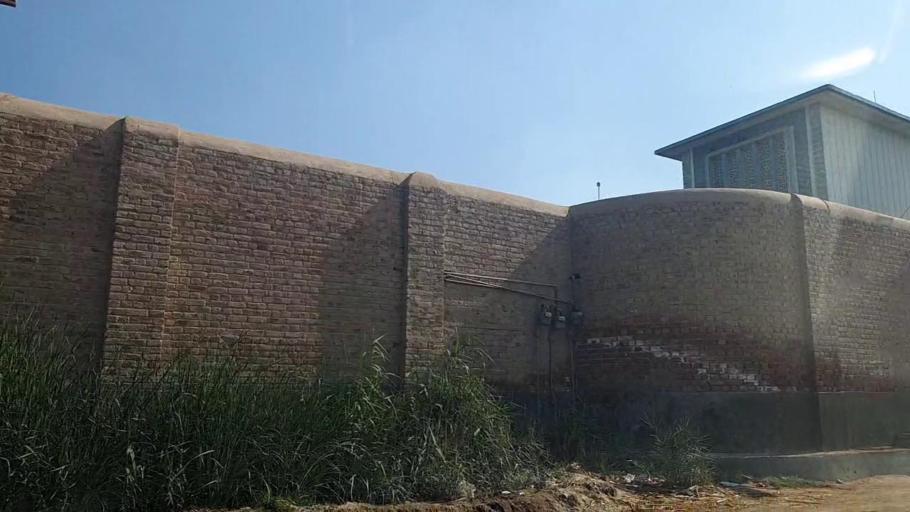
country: PK
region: Sindh
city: Nawabshah
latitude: 26.2483
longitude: 68.3410
